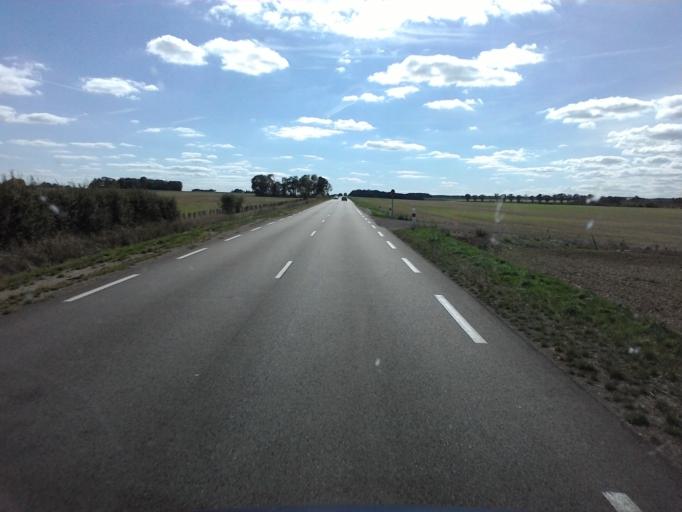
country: FR
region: Bourgogne
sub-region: Departement de la Cote-d'Or
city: Chatillon-sur-Seine
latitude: 47.8486
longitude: 4.5560
